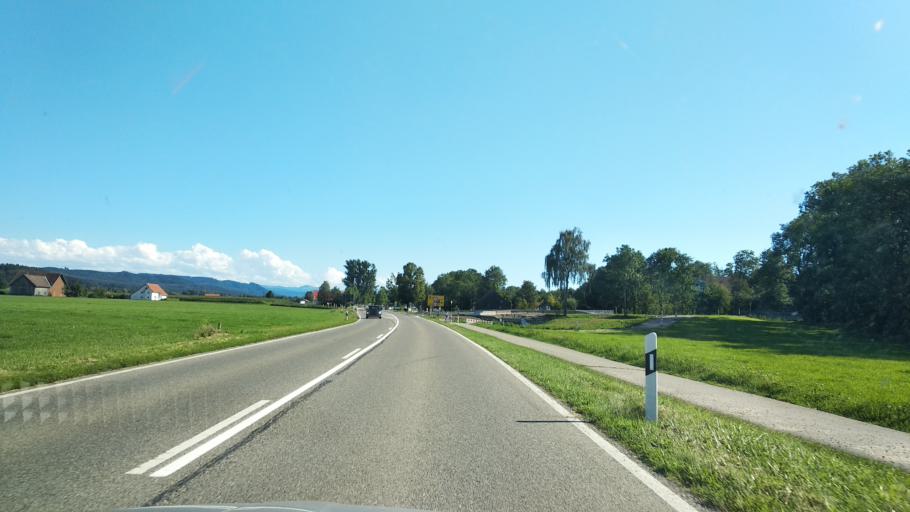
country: DE
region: Baden-Wuerttemberg
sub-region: Tuebingen Region
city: Leutkirch im Allgau
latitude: 47.7912
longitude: 10.0430
